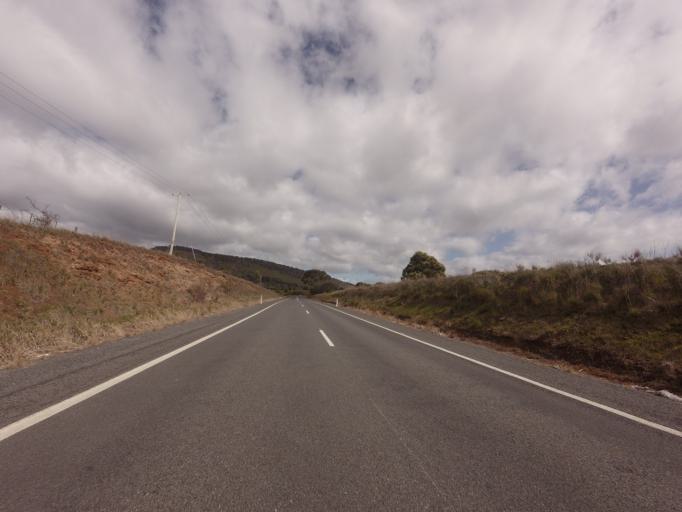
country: AU
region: Tasmania
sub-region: Northern Midlands
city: Evandale
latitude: -41.8135
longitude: 147.5828
